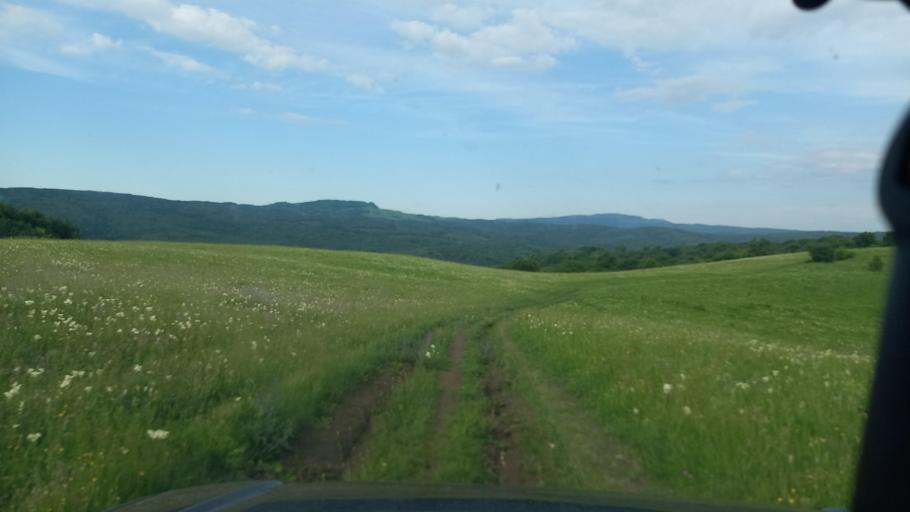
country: RU
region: Karachayevo-Cherkesiya
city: Kurdzhinovo
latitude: 44.1260
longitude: 41.0855
